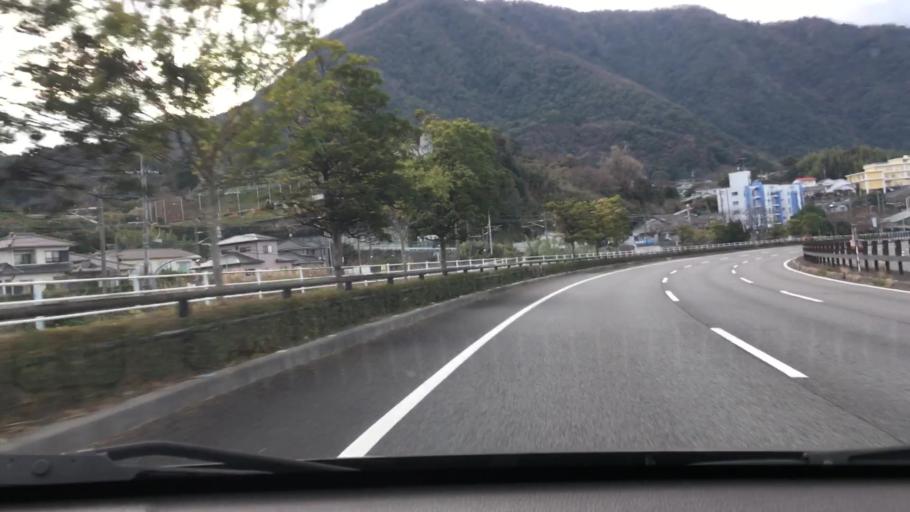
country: JP
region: Oita
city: Beppu
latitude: 33.2551
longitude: 131.5478
